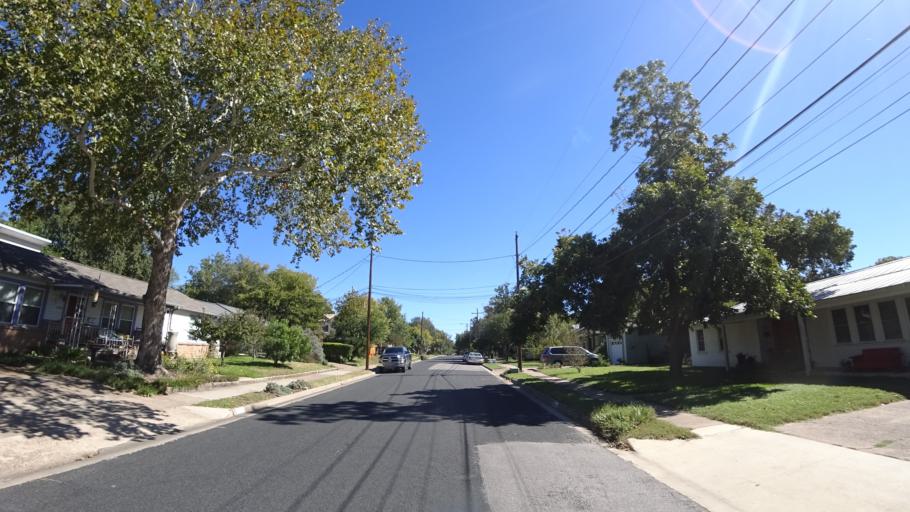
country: US
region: Texas
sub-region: Travis County
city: Austin
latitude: 30.3380
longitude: -97.7298
